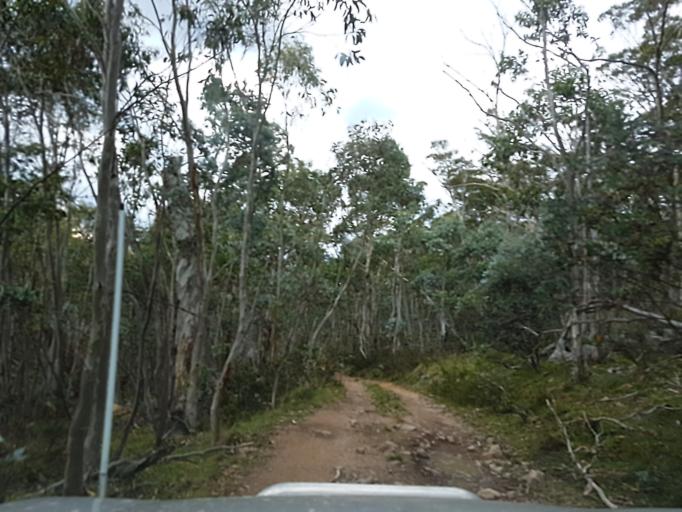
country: AU
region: New South Wales
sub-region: Snowy River
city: Jindabyne
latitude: -36.8821
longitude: 148.1499
